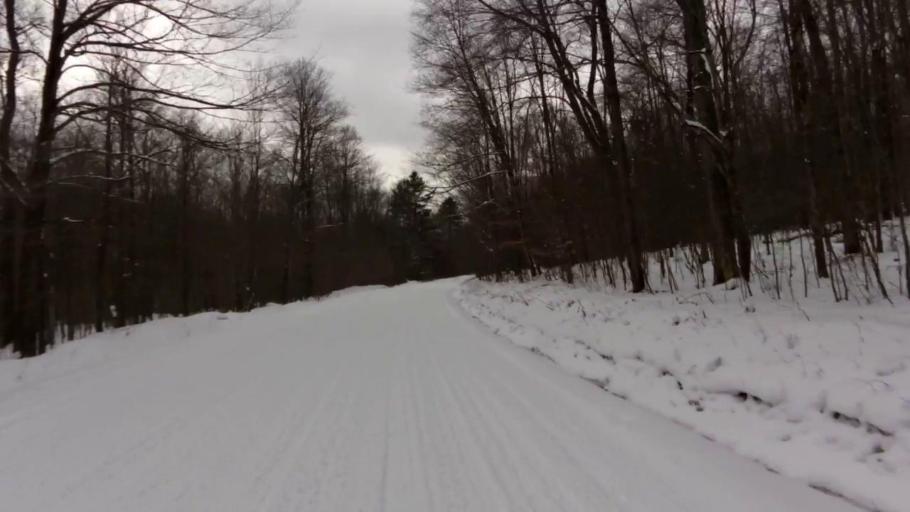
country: US
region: New York
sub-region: Cattaraugus County
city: Salamanca
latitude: 42.0299
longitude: -78.8102
